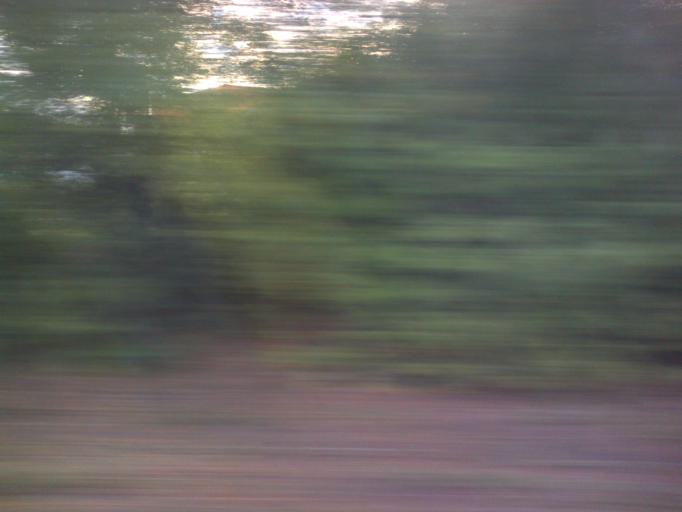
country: RU
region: Moscow
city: Nagornyy
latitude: 55.6332
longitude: 37.6266
